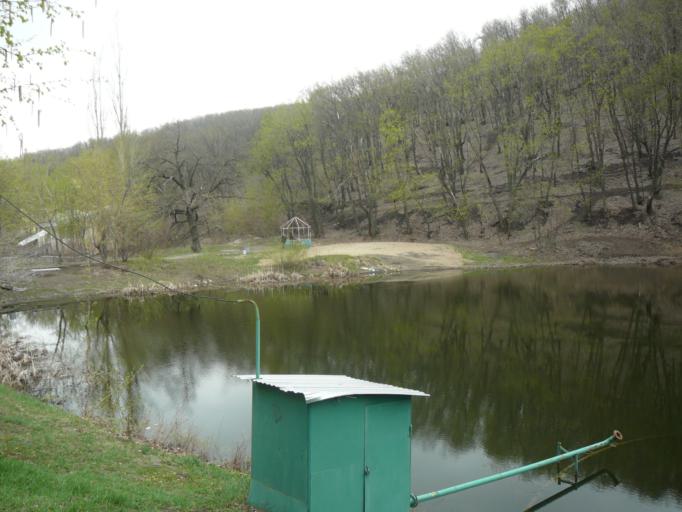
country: RU
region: Saratov
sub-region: Saratovskiy Rayon
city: Saratov
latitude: 51.5477
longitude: 45.9588
